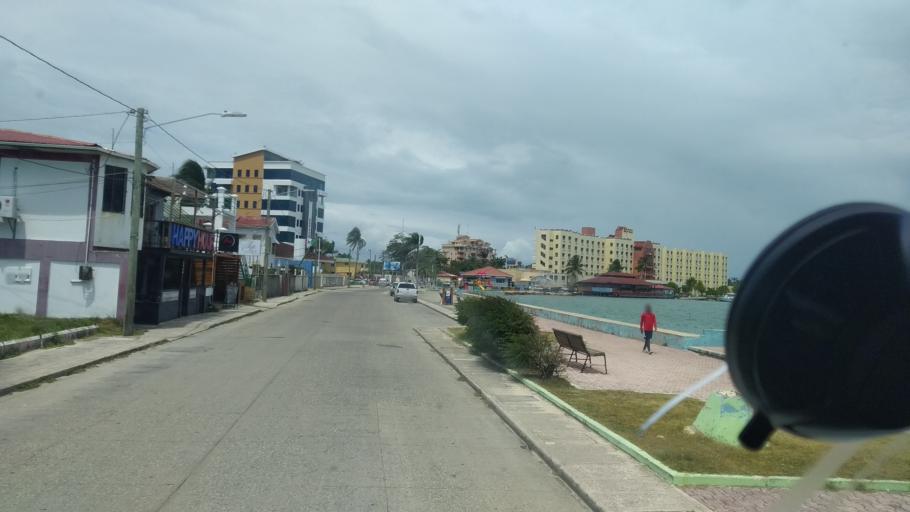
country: BZ
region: Belize
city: Belize City
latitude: 17.5024
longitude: -88.1870
